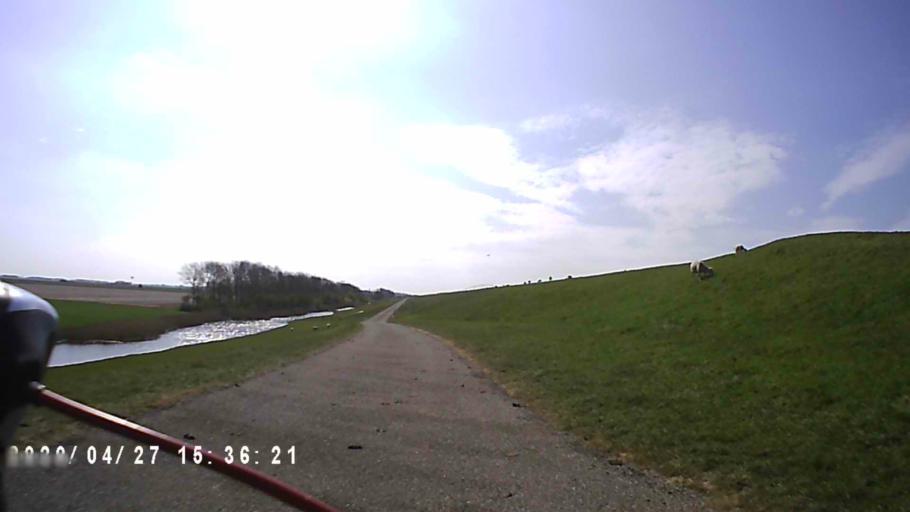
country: NL
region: Groningen
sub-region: Gemeente De Marne
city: Ulrum
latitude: 53.3979
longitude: 6.3282
